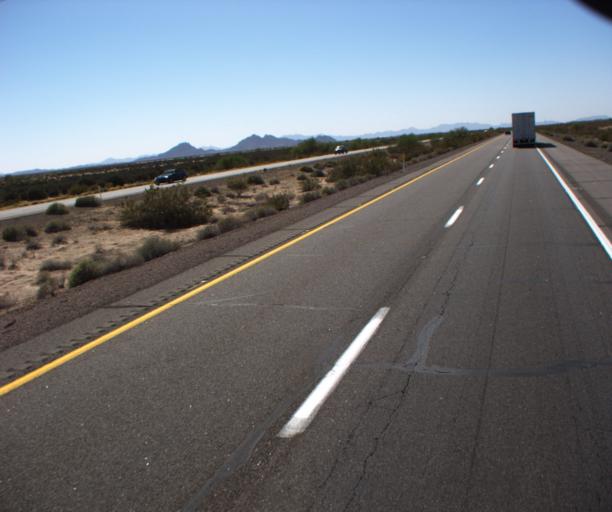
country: US
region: Arizona
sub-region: Yuma County
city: Wellton
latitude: 32.7025
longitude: -113.8954
